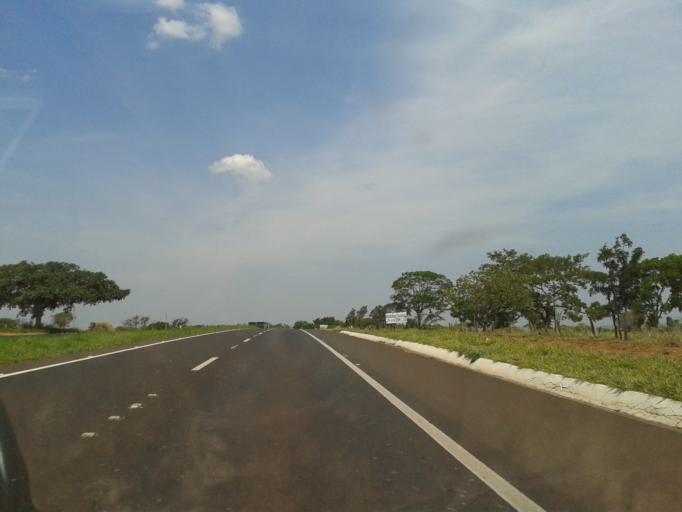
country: BR
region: Minas Gerais
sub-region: Monte Alegre De Minas
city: Monte Alegre de Minas
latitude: -18.8795
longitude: -48.7432
